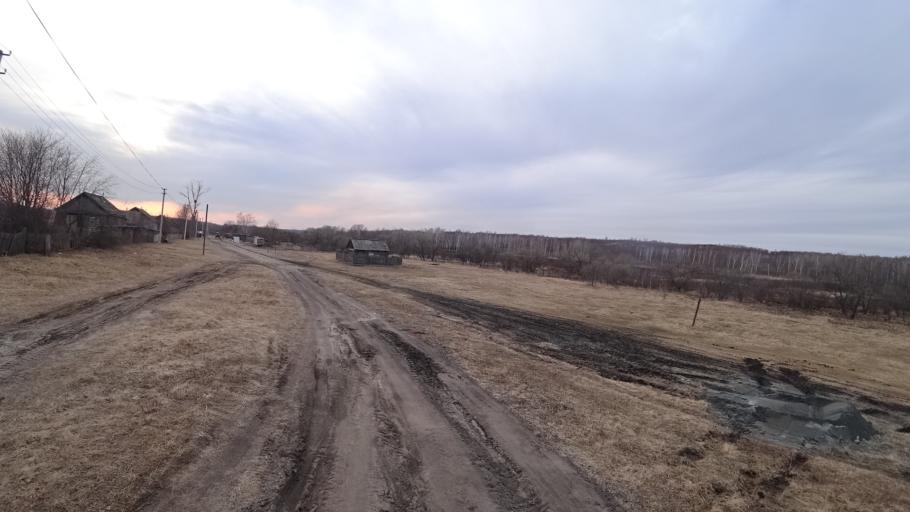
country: RU
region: Amur
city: Bureya
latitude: 50.0218
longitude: 129.7706
